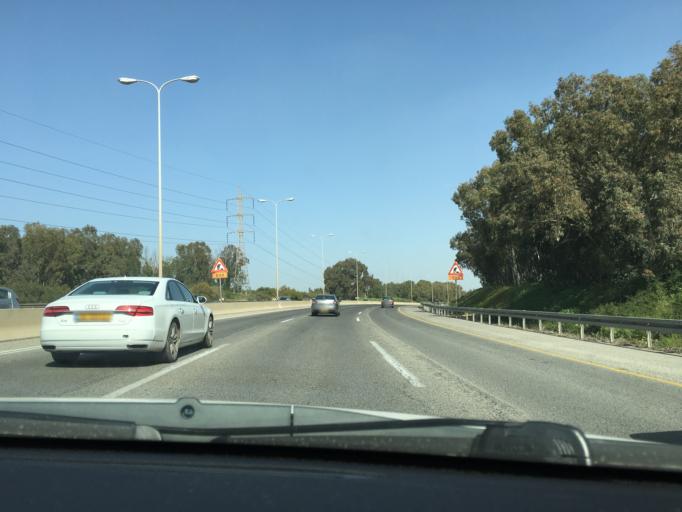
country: IL
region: Central District
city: Hod HaSharon
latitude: 32.1552
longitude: 34.8728
